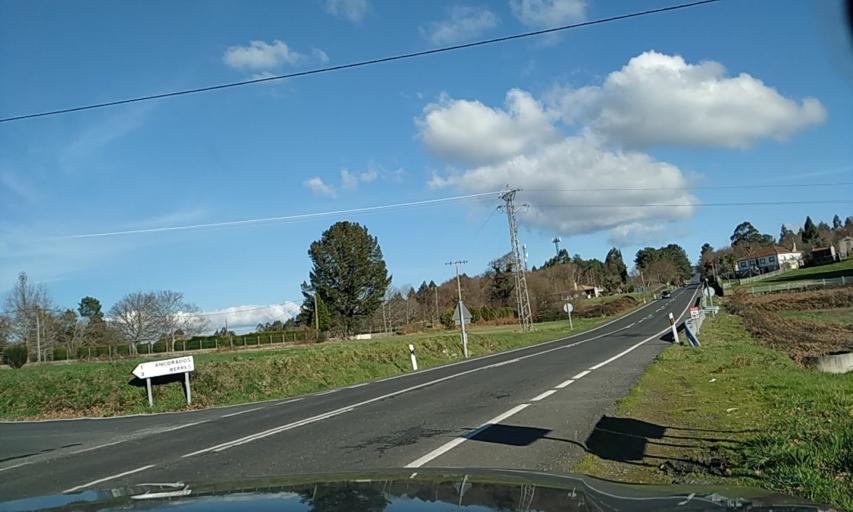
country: ES
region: Galicia
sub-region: Provincia da Coruna
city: Ribeira
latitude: 42.7071
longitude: -8.4166
